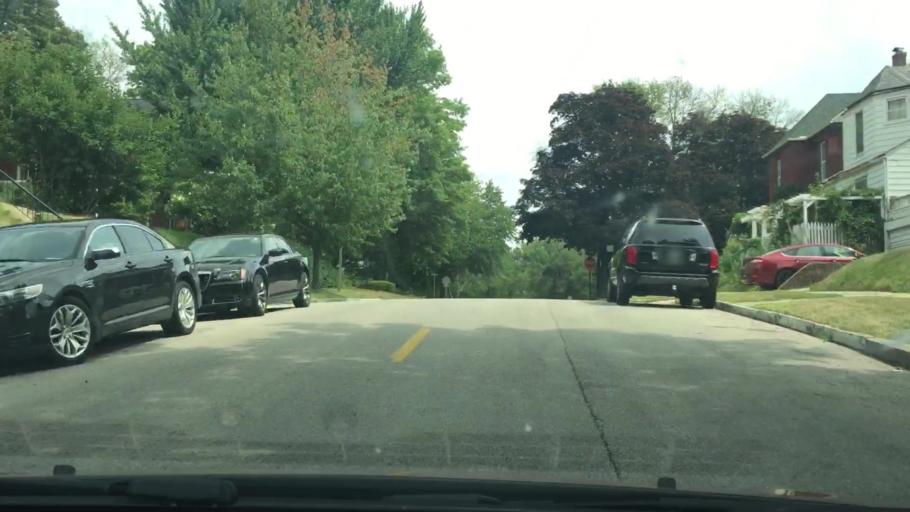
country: US
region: Iowa
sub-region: Muscatine County
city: Muscatine
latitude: 41.4175
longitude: -91.0547
